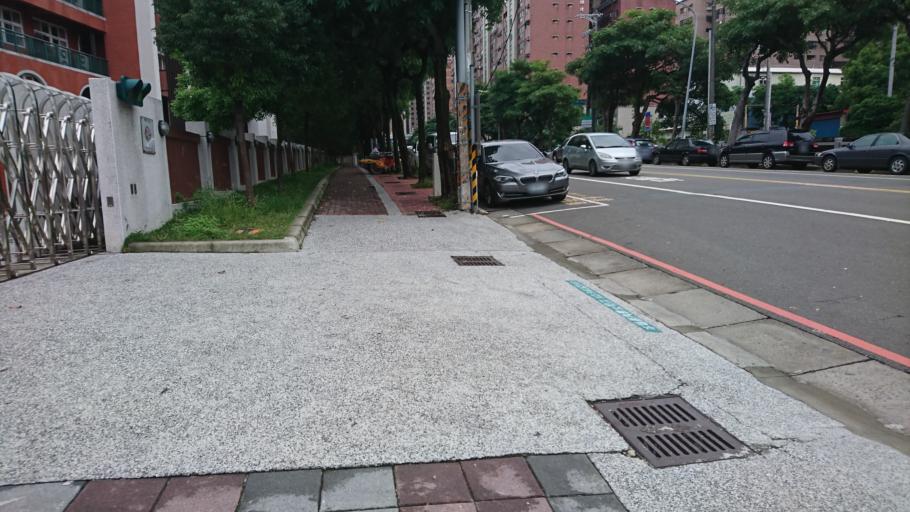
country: TW
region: Taiwan
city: Taoyuan City
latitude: 25.0521
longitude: 121.2973
